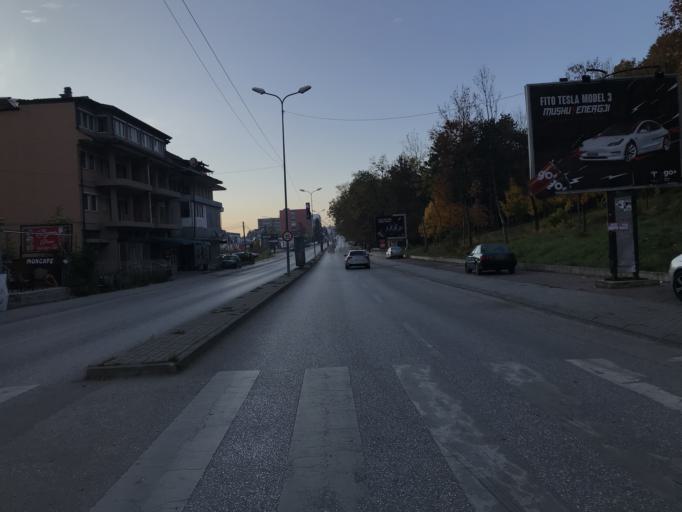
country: XK
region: Pec
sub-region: Komuna e Pejes
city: Peje
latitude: 42.6543
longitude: 20.2926
